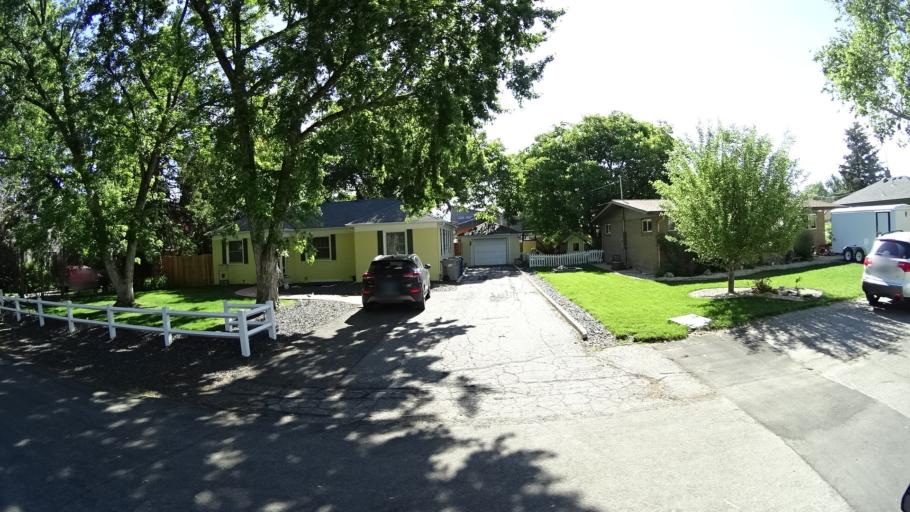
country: US
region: Idaho
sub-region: Ada County
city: Garden City
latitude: 43.6198
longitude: -116.2408
